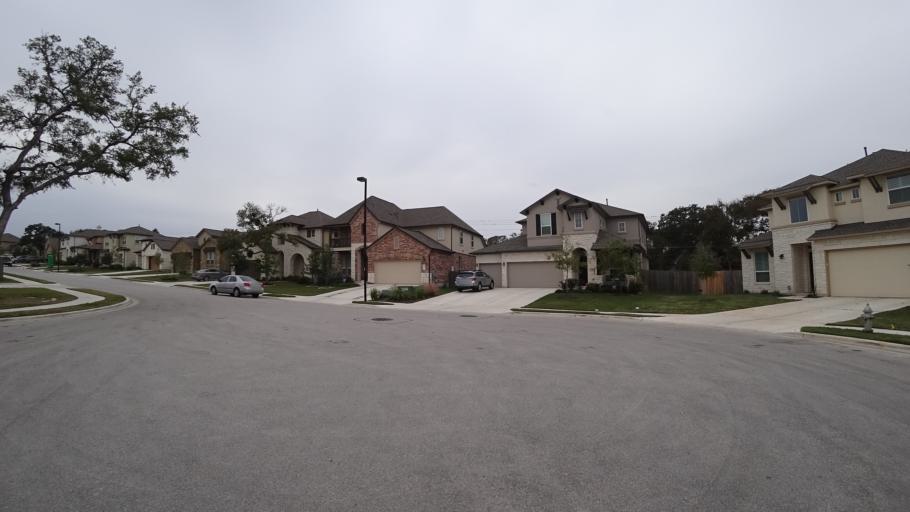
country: US
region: Texas
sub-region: Travis County
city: Shady Hollow
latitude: 30.1846
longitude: -97.8993
